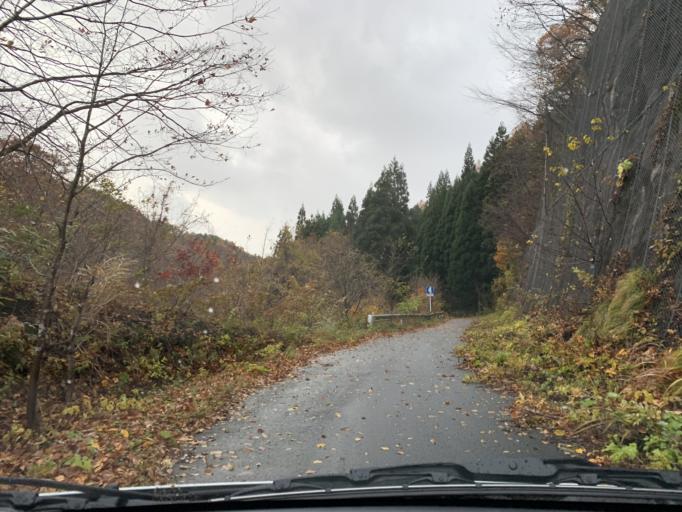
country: JP
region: Iwate
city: Mizusawa
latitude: 39.0977
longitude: 140.9382
